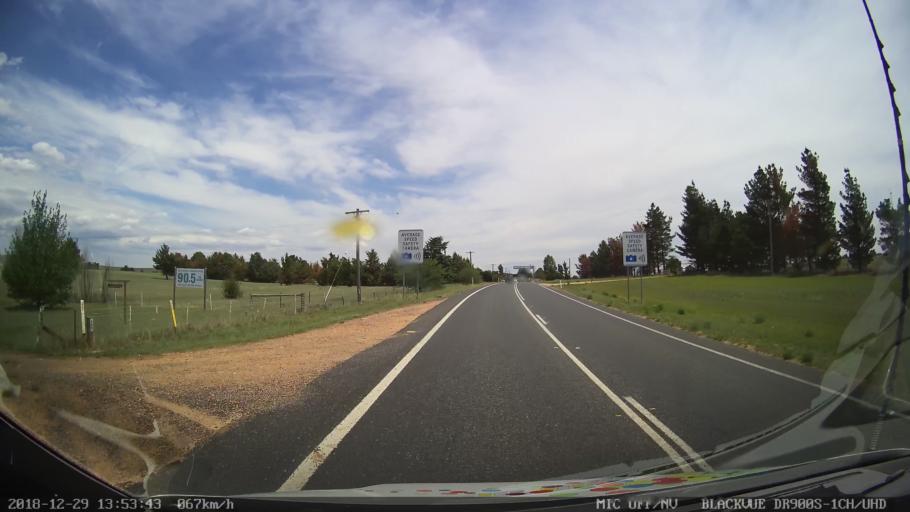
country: AU
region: New South Wales
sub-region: Cooma-Monaro
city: Cooma
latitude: -36.2091
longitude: 149.1565
